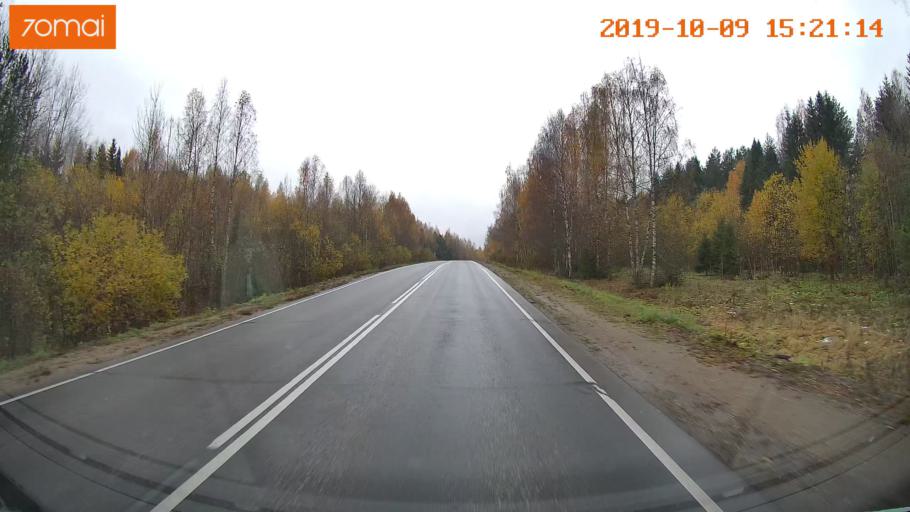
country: RU
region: Kostroma
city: Susanino
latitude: 58.0556
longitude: 41.5234
